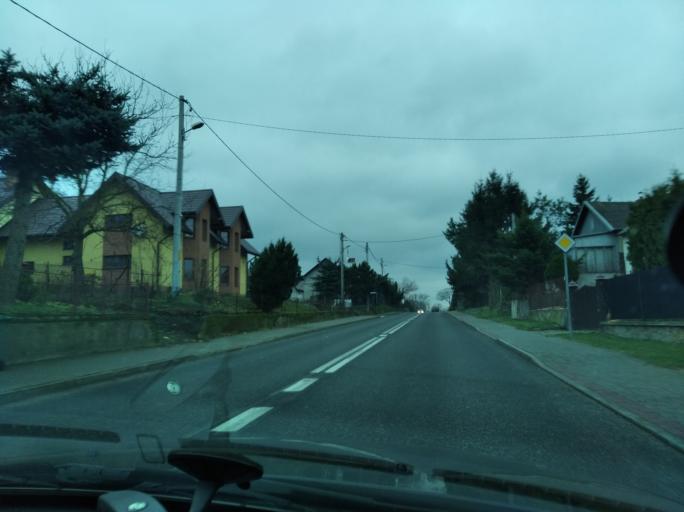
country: PL
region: Subcarpathian Voivodeship
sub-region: Powiat przeworski
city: Kanczuga
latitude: 49.9838
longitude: 22.4056
